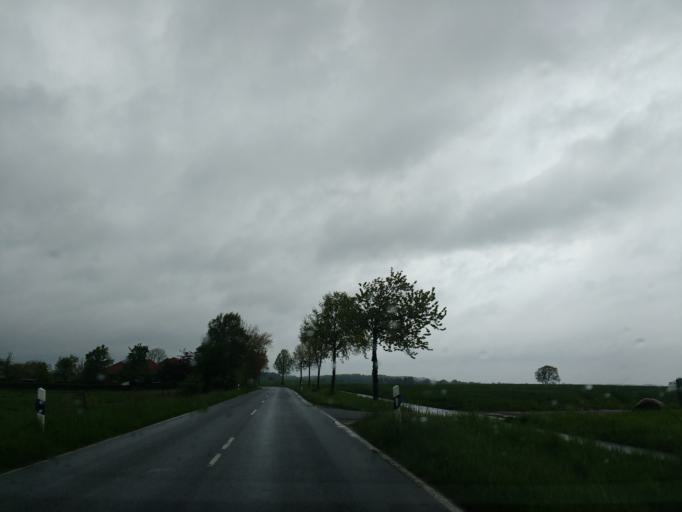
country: DE
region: Schleswig-Holstein
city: Waabs
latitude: 54.5553
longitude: 9.9891
